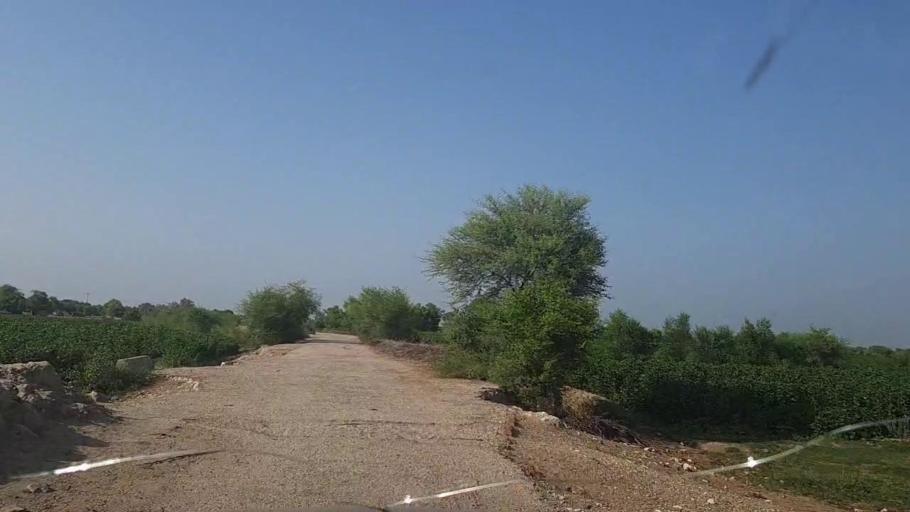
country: PK
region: Sindh
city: Khanpur
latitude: 27.7120
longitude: 69.3320
